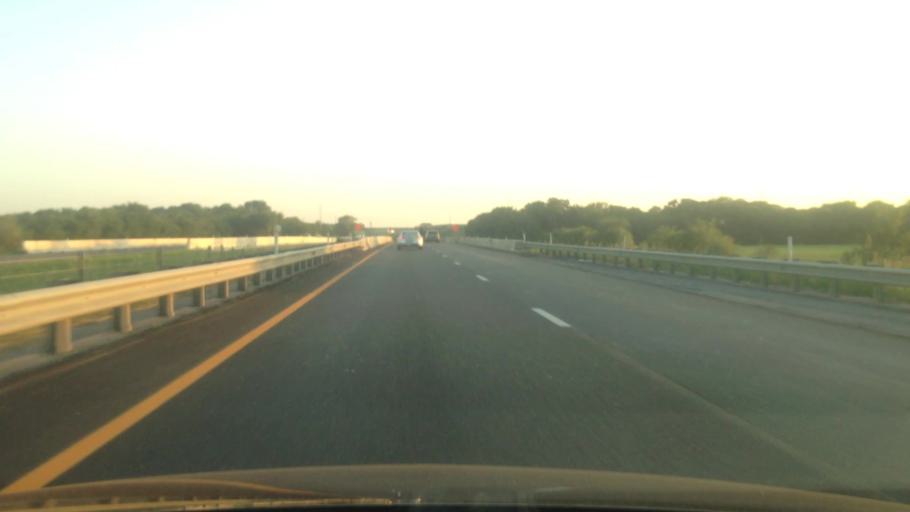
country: US
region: Texas
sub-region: Denton County
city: Denton
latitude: 33.1794
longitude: -97.1767
